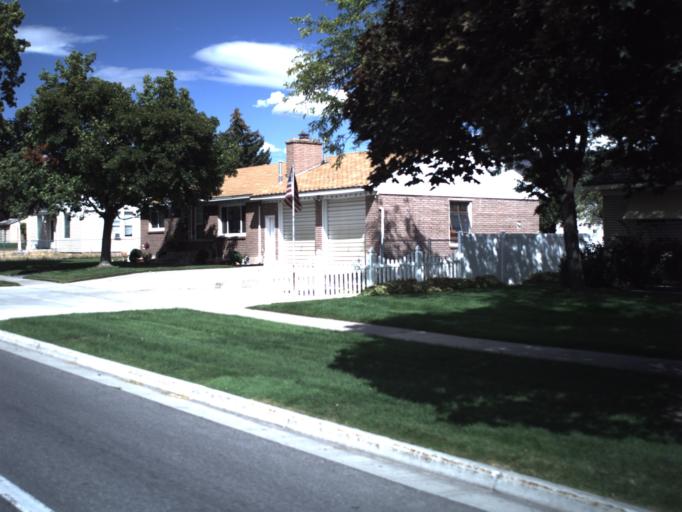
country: US
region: Utah
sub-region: Cache County
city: Smithfield
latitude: 41.8273
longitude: -111.8328
